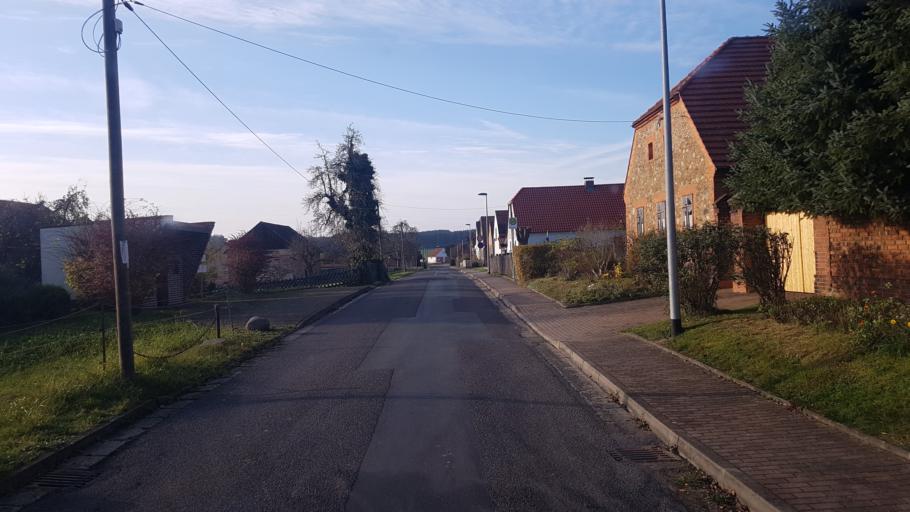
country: DE
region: Brandenburg
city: Calau
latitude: 51.6905
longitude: 13.9697
